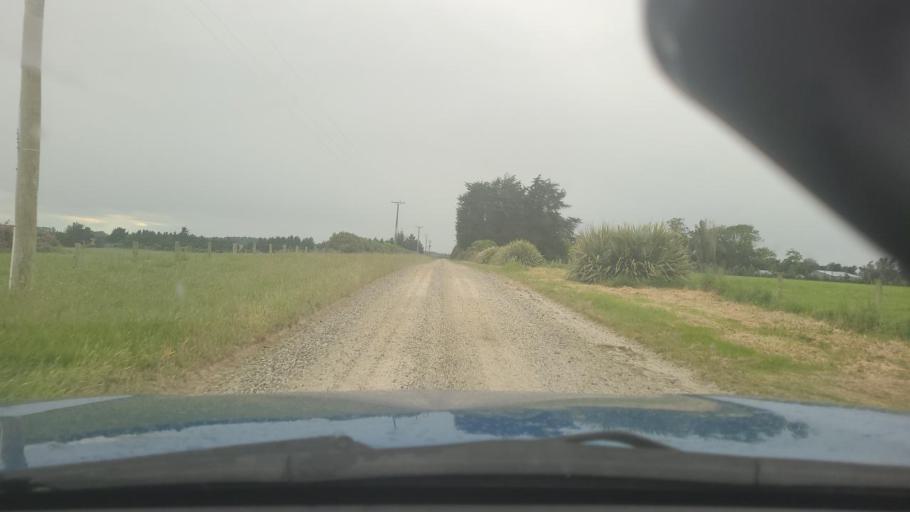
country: NZ
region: Southland
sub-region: Invercargill City
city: Invercargill
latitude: -46.3924
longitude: 168.5650
